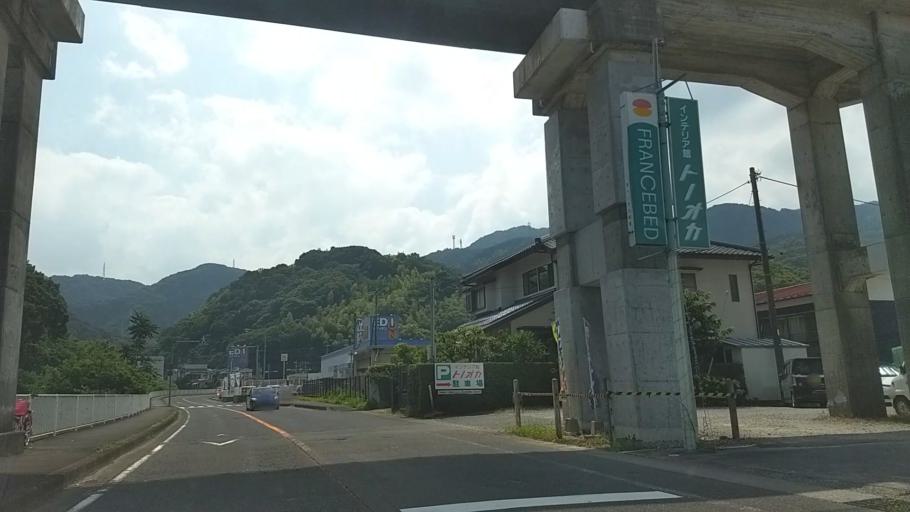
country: JP
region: Shizuoka
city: Ito
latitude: 34.9532
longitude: 139.0880
